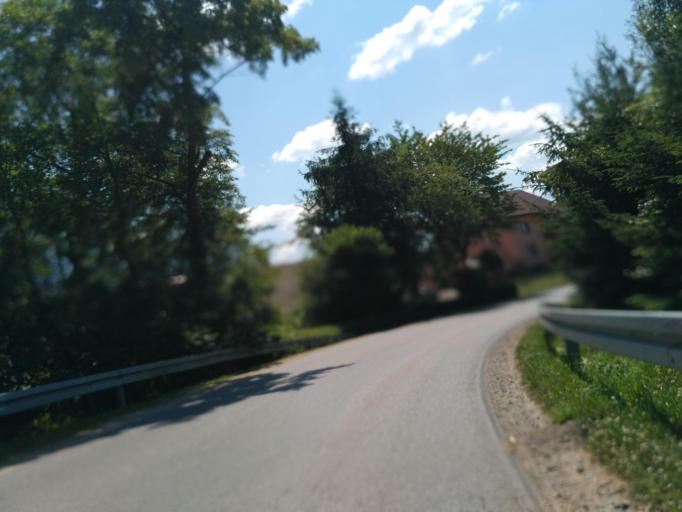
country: PL
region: Subcarpathian Voivodeship
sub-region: Powiat sanocki
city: Niebieszczany
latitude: 49.4980
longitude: 22.1660
